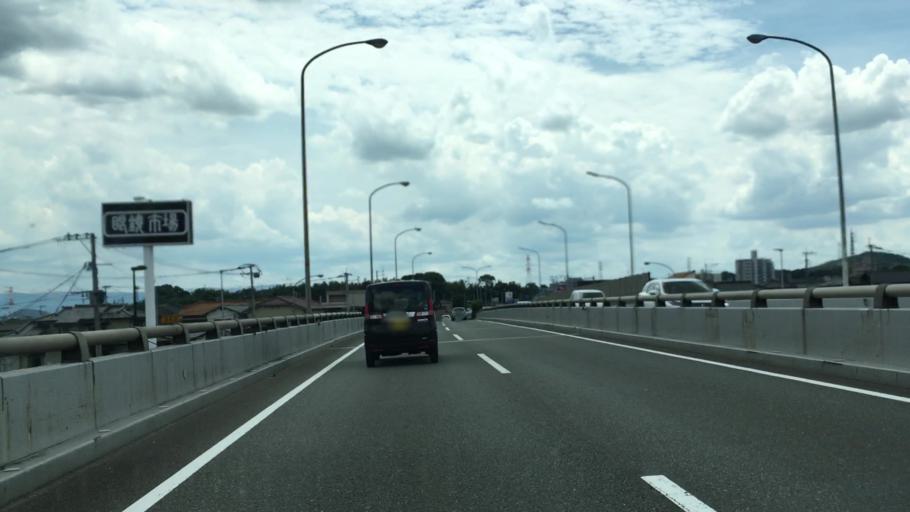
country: JP
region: Fukuoka
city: Chikushino-shi
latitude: 33.4831
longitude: 130.5380
